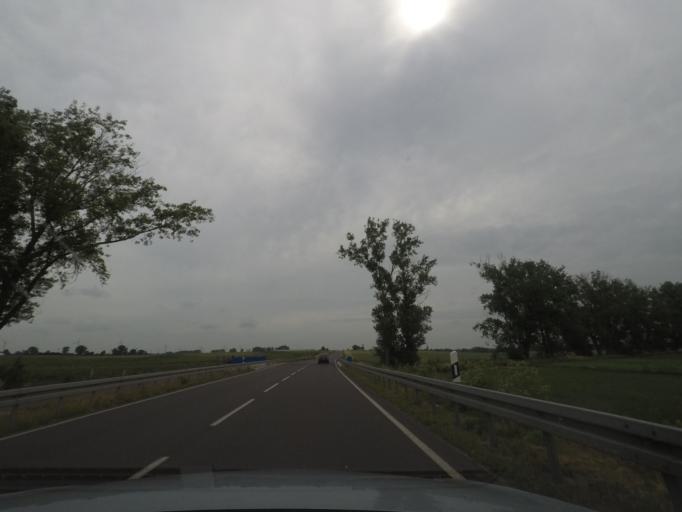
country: DE
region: Saxony-Anhalt
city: Hadmersleben
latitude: 52.0143
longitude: 11.3173
